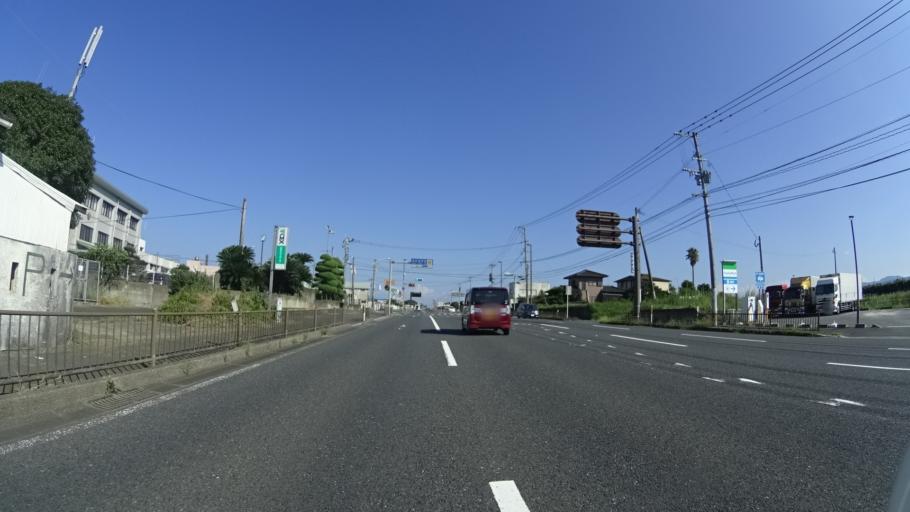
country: JP
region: Fukuoka
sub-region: Buzen-shi
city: Buzen
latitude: 33.6056
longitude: 131.1182
